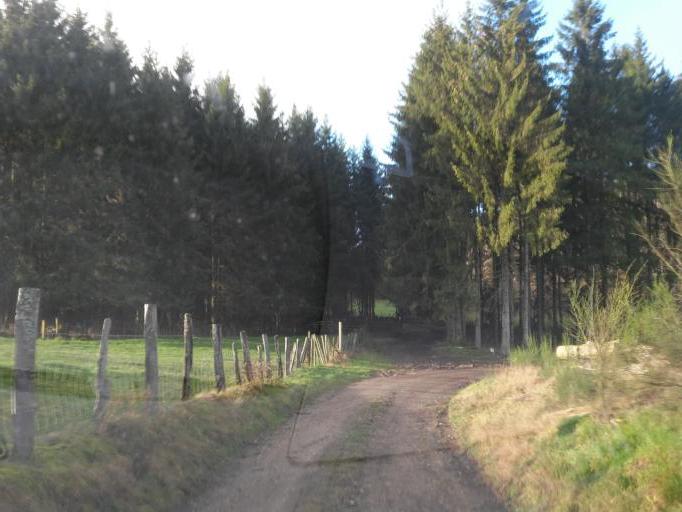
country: BE
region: Wallonia
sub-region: Province du Luxembourg
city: Neufchateau
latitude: 49.8041
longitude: 5.4317
